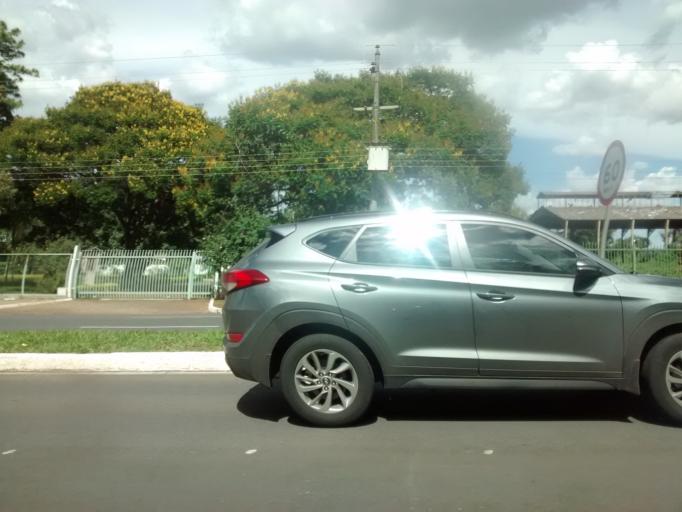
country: BR
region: Federal District
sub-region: Brasilia
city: Brasilia
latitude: -15.7500
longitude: -47.8812
